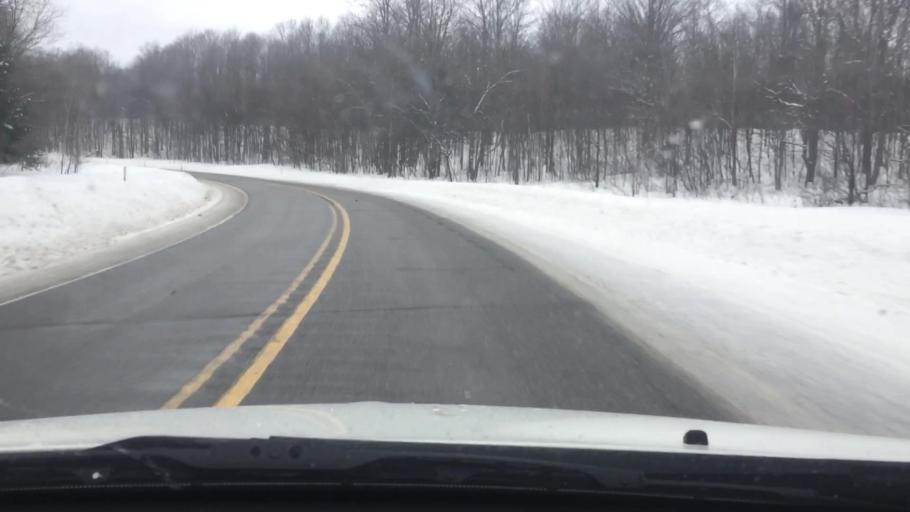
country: US
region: Michigan
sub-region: Charlevoix County
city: Boyne City
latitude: 45.0852
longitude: -84.9263
